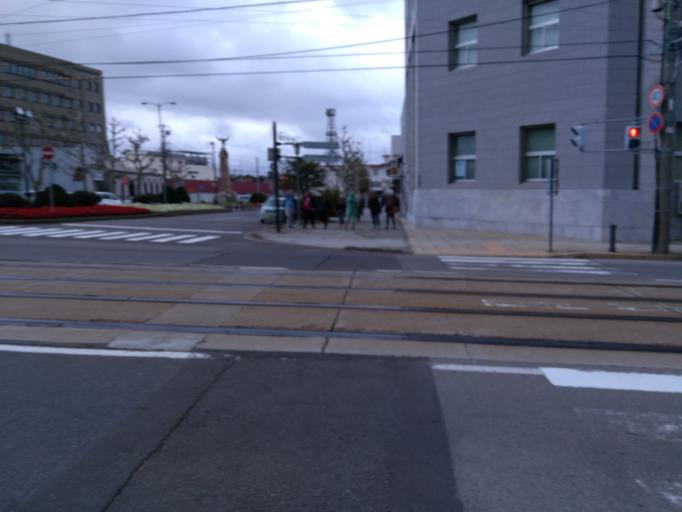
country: JP
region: Hokkaido
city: Hakodate
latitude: 41.7671
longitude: 140.7116
